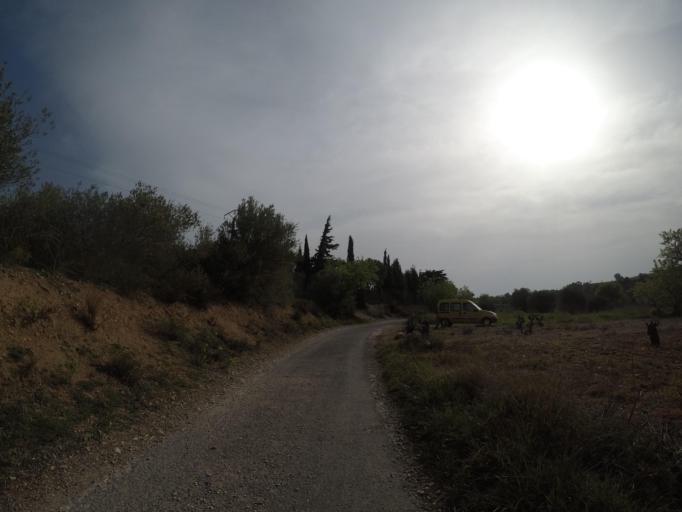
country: FR
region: Languedoc-Roussillon
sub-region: Departement des Pyrenees-Orientales
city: Baixas
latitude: 42.7455
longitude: 2.8043
